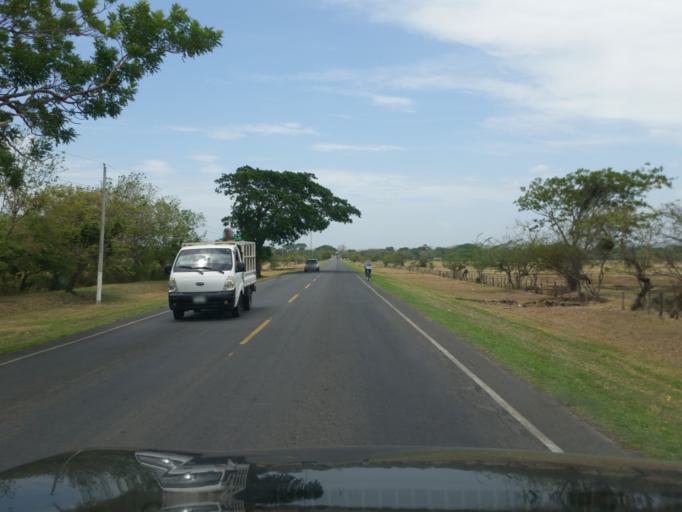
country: NI
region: Granada
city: Nandaime
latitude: 11.6668
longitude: -85.9764
